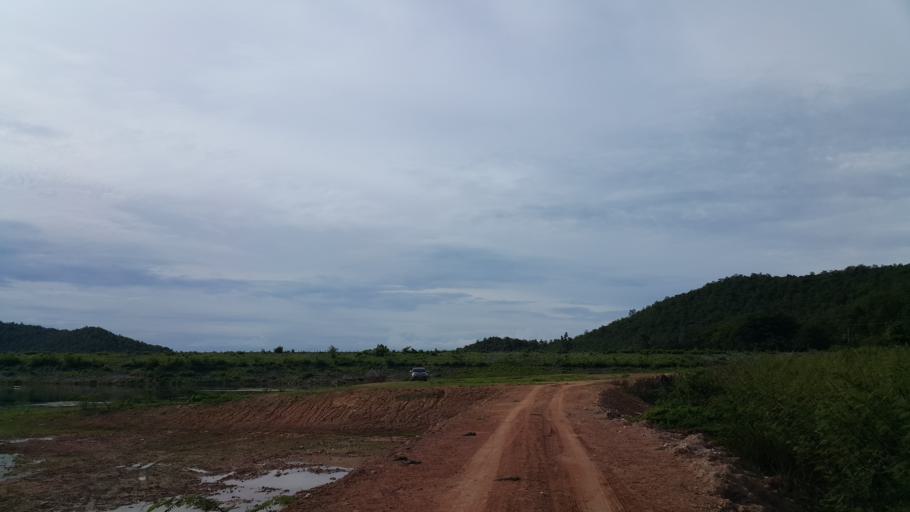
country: TH
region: Chiang Mai
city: Mae On
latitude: 18.7038
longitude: 99.2055
